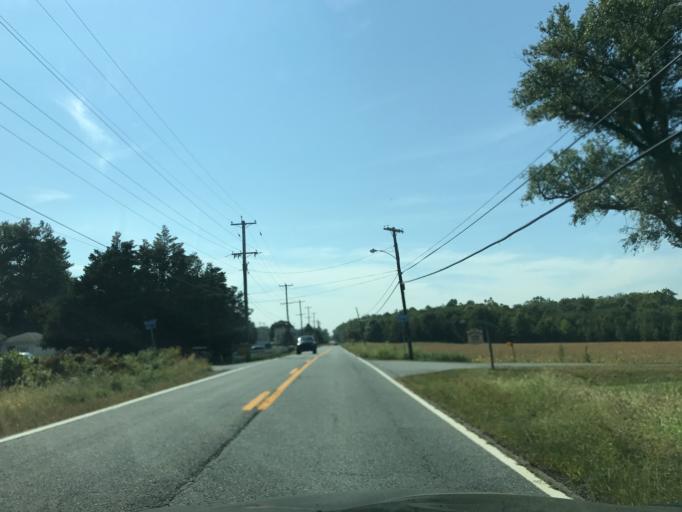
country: US
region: Maryland
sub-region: Cecil County
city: Perryville
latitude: 39.5663
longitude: -76.0581
